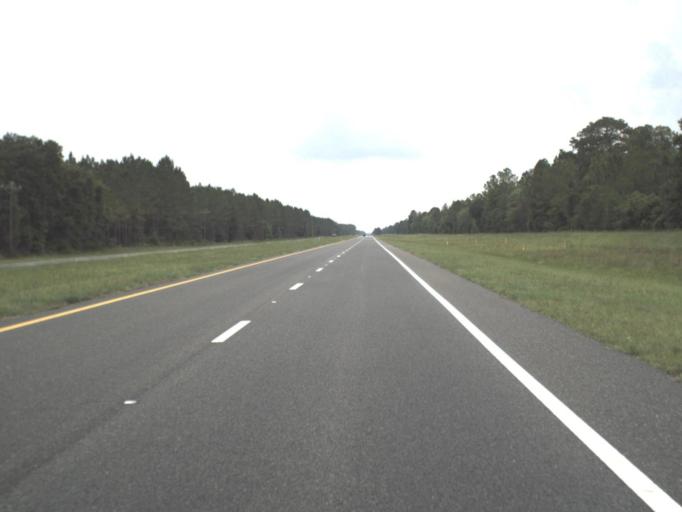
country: US
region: Florida
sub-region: Levy County
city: Chiefland
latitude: 29.3867
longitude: -82.8047
